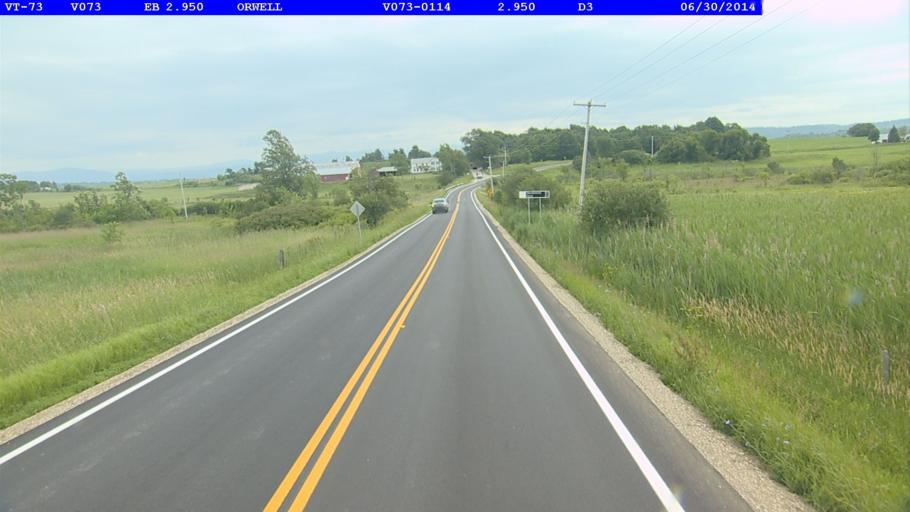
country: US
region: Vermont
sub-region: Rutland County
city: Brandon
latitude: 43.8016
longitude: -73.2482
